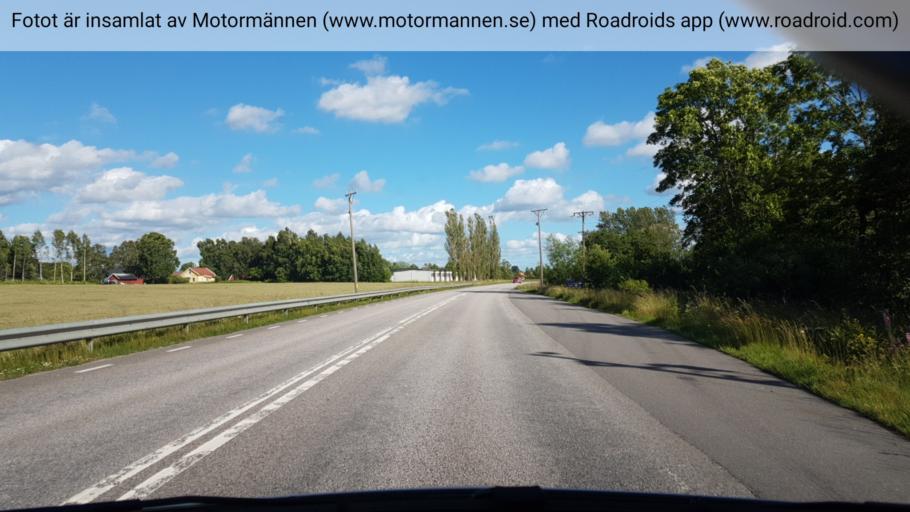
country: SE
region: Vaestra Goetaland
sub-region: Vara Kommun
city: Kvanum
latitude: 58.2554
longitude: 13.0732
